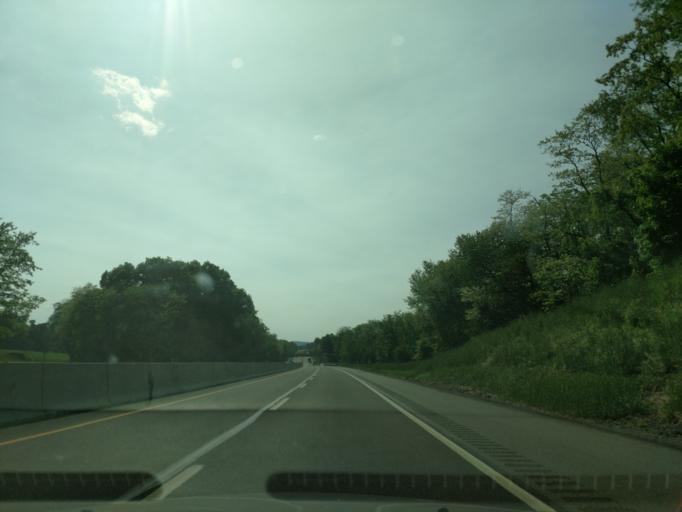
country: US
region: Pennsylvania
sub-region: Lancaster County
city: Schoeneck
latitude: 40.2438
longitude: -76.1562
